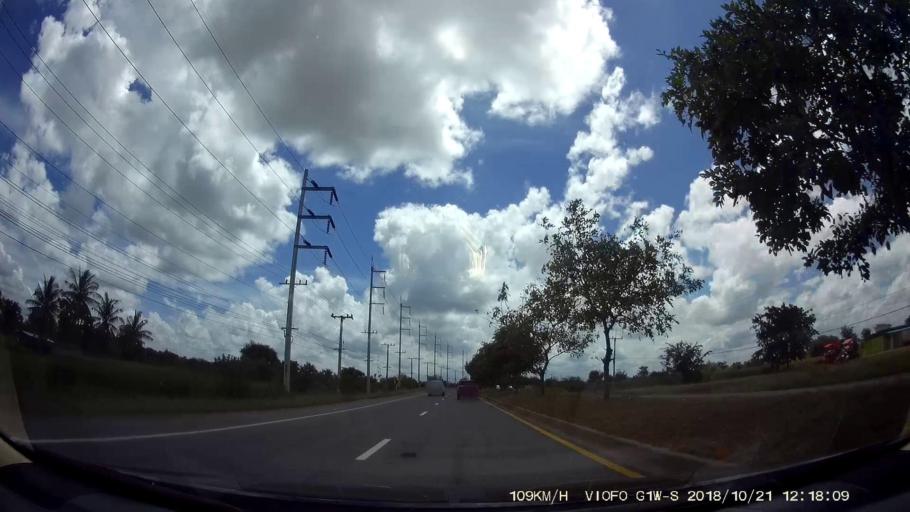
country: TH
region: Nakhon Ratchasima
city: Dan Khun Thot
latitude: 15.3206
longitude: 101.8180
